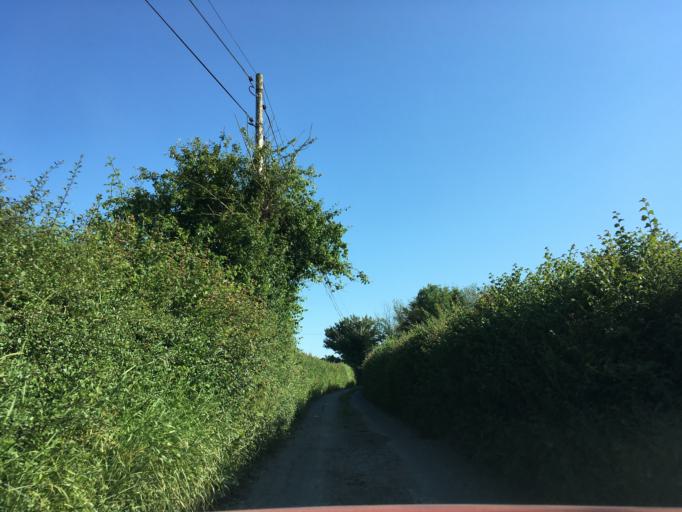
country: GB
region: England
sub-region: South Gloucestershire
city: Siston
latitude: 51.4665
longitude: -2.4374
